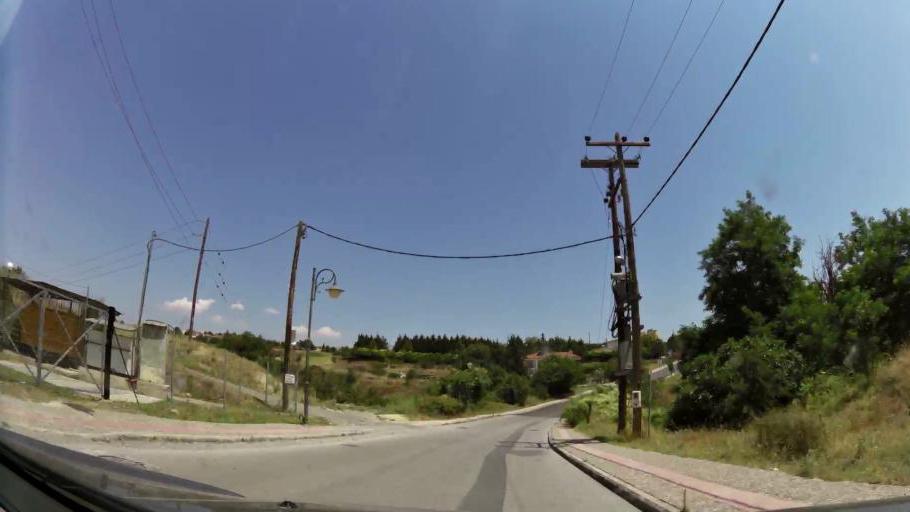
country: GR
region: Central Macedonia
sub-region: Nomos Thessalonikis
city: Plagiari
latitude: 40.4699
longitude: 22.9632
